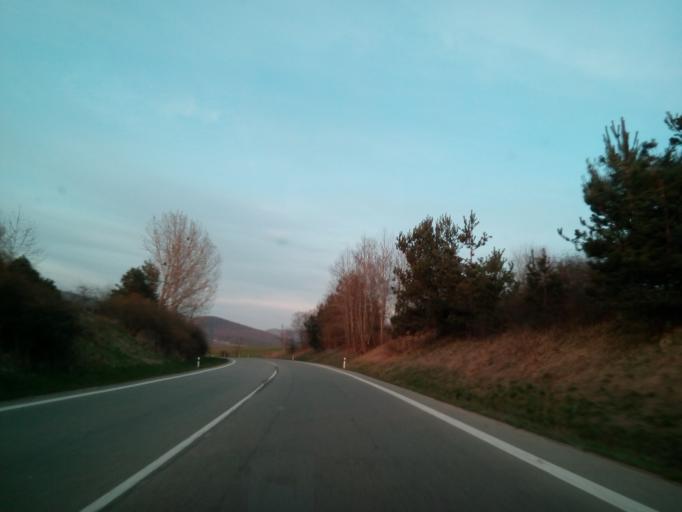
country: SK
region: Kosicky
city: Roznava
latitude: 48.6424
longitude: 20.5318
